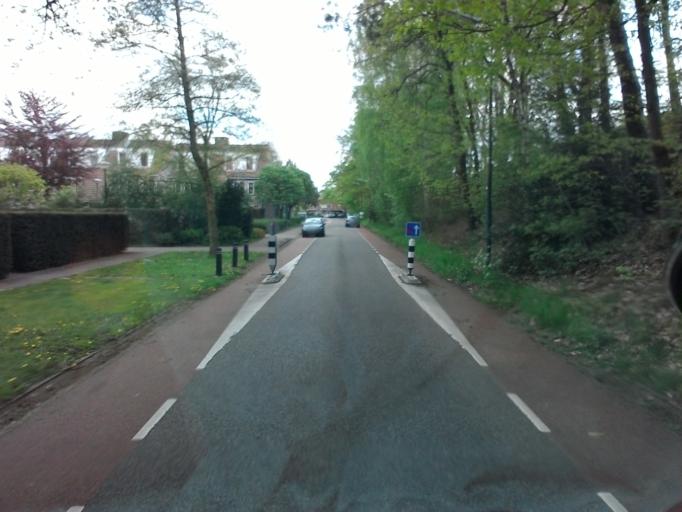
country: NL
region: Utrecht
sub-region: Gemeente Utrechtse Heuvelrug
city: Maarn
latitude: 52.0656
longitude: 5.3647
